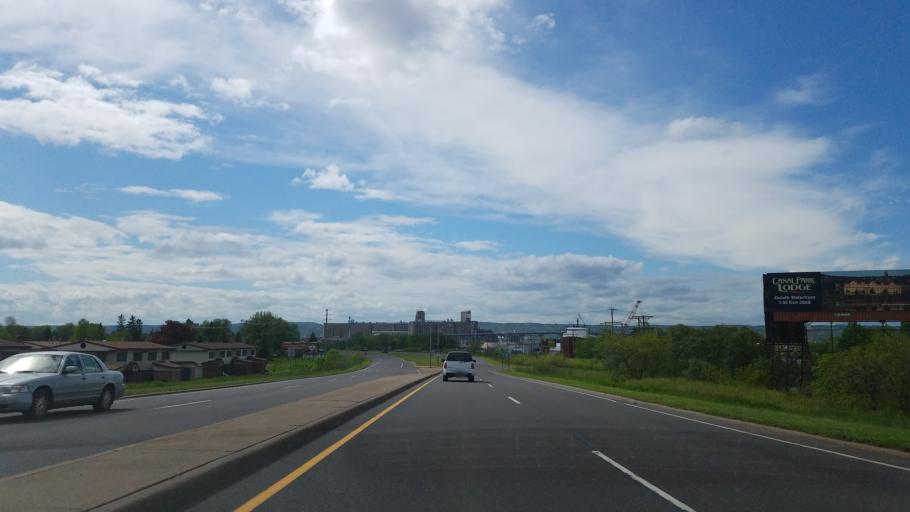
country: US
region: Wisconsin
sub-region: Douglas County
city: Superior
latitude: 46.7315
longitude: -92.0831
